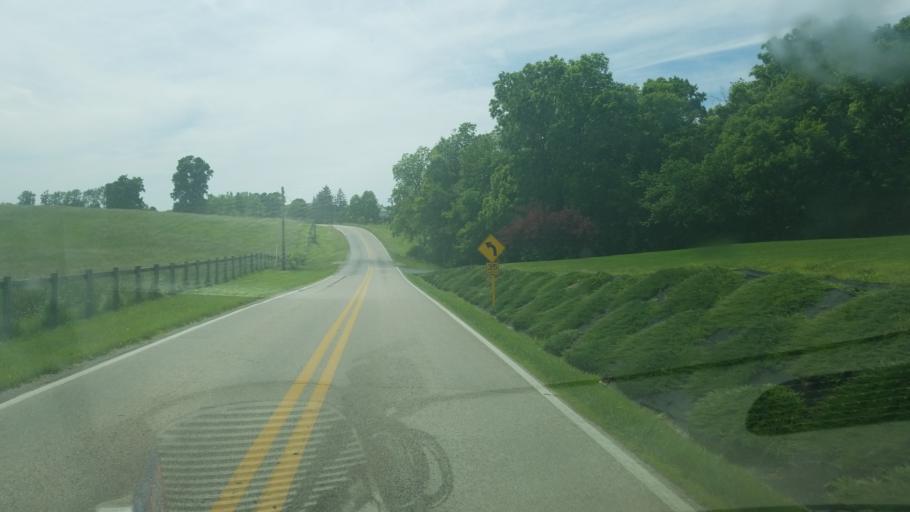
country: US
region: Ohio
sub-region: Delaware County
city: Delaware
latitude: 40.3357
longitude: -83.0474
